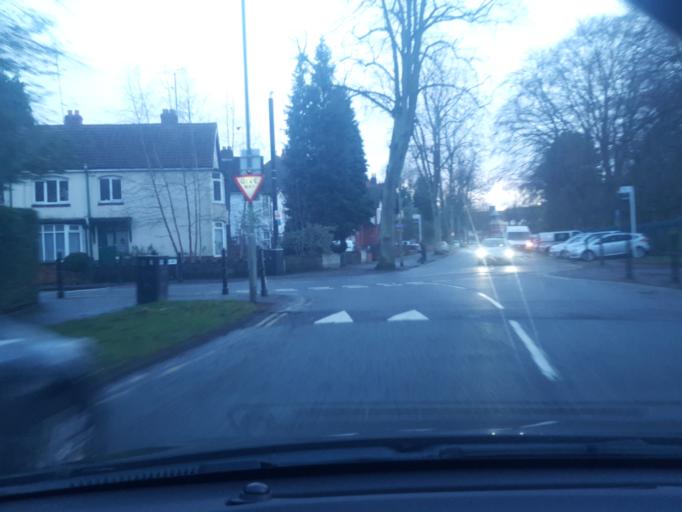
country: GB
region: England
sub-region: Wolverhampton
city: Wolverhampton
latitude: 52.5901
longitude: -2.1368
